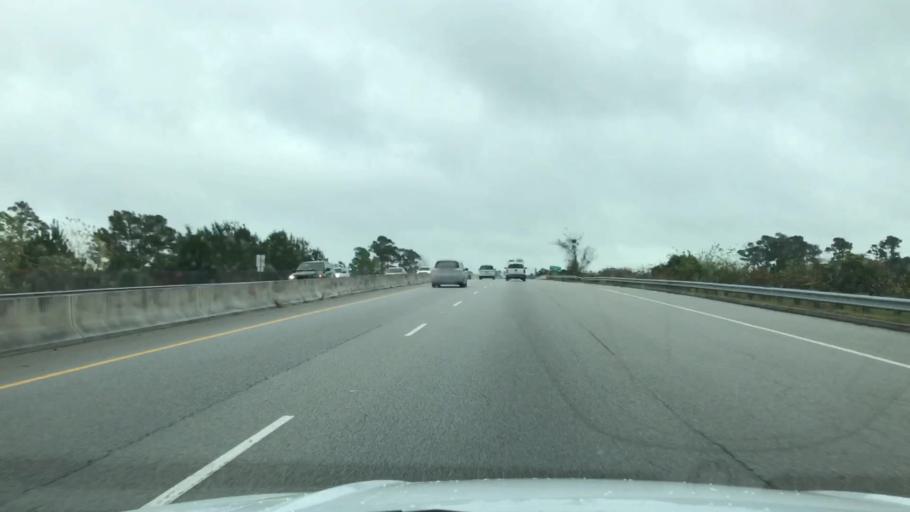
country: US
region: South Carolina
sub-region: Horry County
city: Myrtle Beach
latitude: 33.7513
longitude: -78.8505
